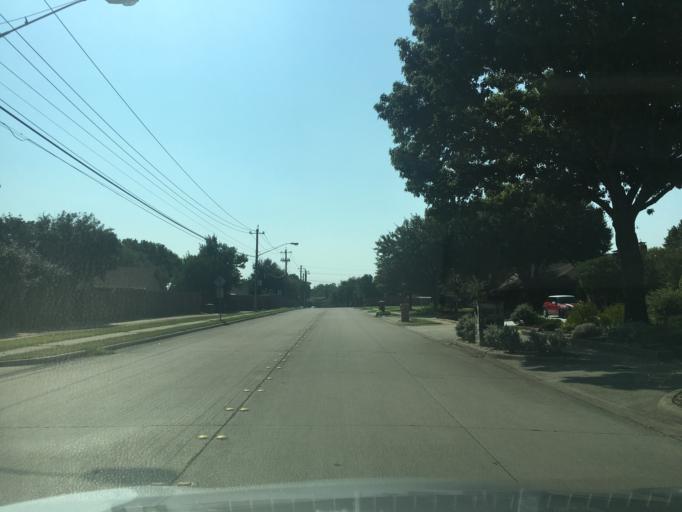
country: US
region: Texas
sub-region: Dallas County
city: Garland
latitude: 32.9428
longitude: -96.6343
